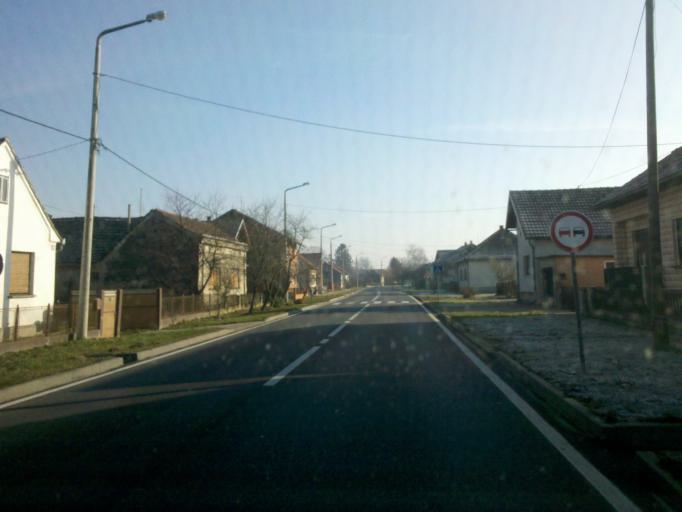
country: HR
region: Koprivnicko-Krizevacka
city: Virje
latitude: 46.0877
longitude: 16.9468
